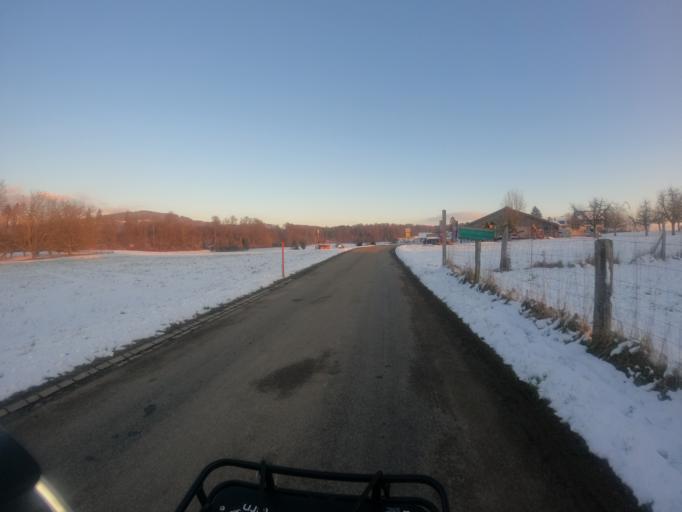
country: CH
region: Zurich
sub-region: Bezirk Affoltern
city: Affoltern / Hasenbueel
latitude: 47.2658
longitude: 8.4537
